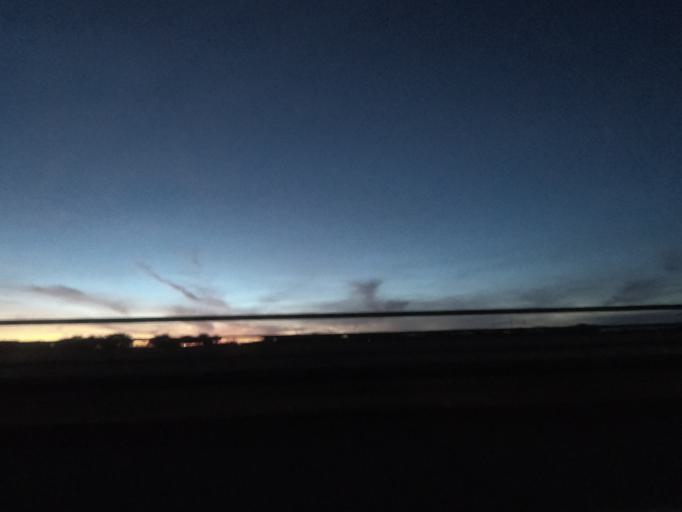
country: PT
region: Santarem
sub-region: Benavente
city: Benavente
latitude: 38.9338
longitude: -8.8186
